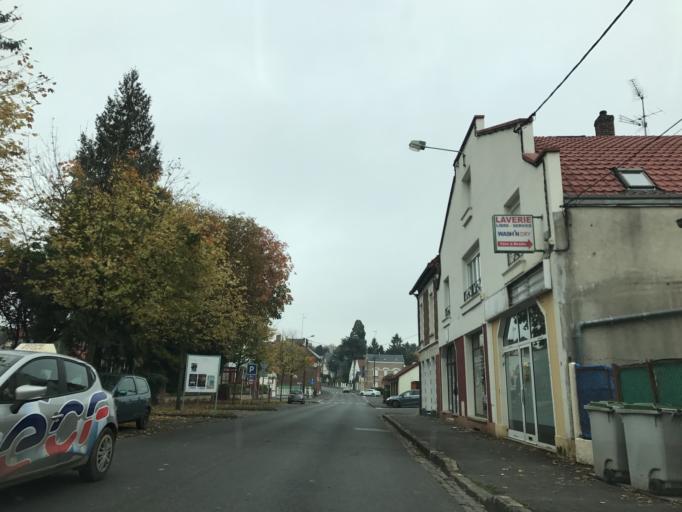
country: FR
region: Picardie
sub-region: Departement de la Somme
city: Peronne
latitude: 49.9300
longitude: 2.9322
